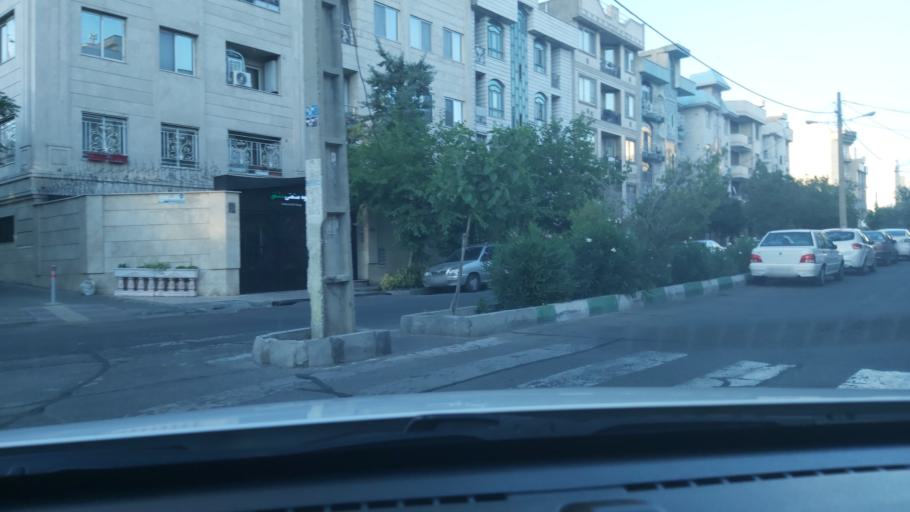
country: IR
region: Tehran
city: Tehran
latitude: 35.7315
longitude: 51.3053
